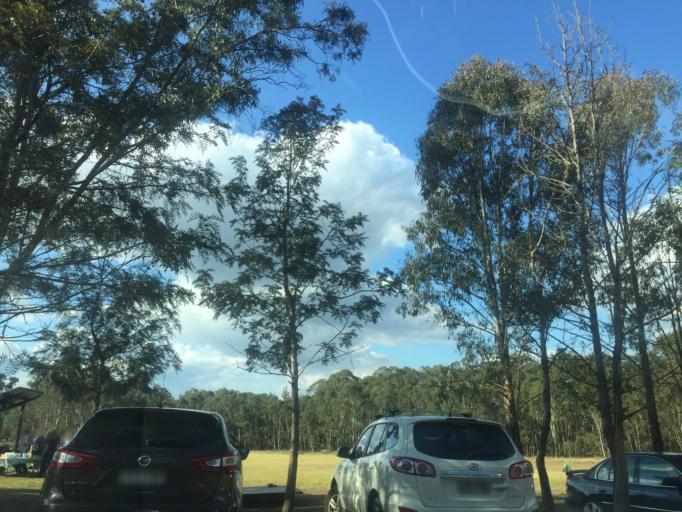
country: AU
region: New South Wales
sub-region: Blacktown
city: Rouse Hill
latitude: -33.6802
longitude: 150.9107
